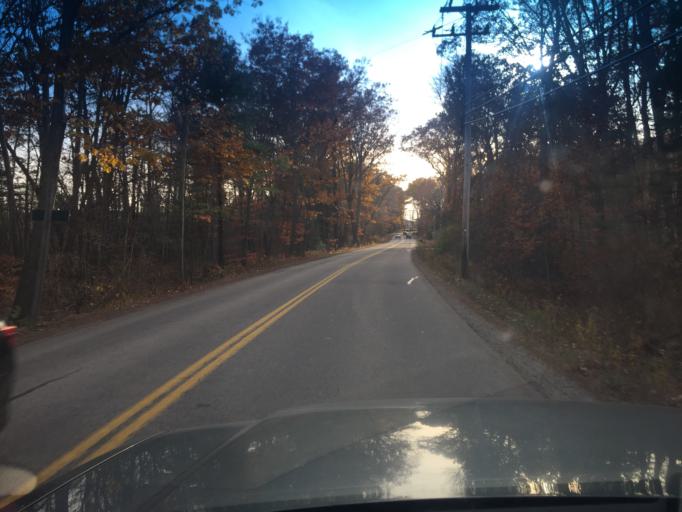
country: US
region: Maine
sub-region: York County
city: York Beach
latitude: 43.1587
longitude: -70.6305
